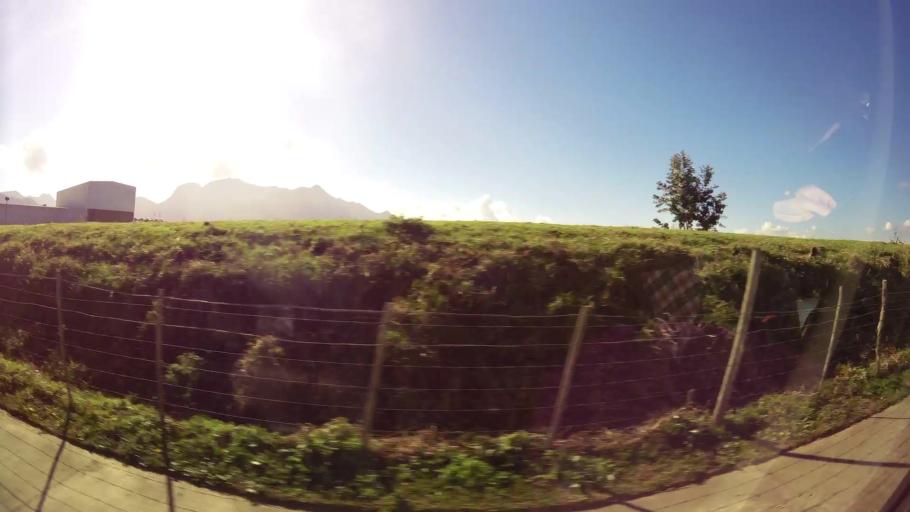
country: ZA
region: Western Cape
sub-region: Eden District Municipality
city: George
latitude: -33.9566
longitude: 22.3983
